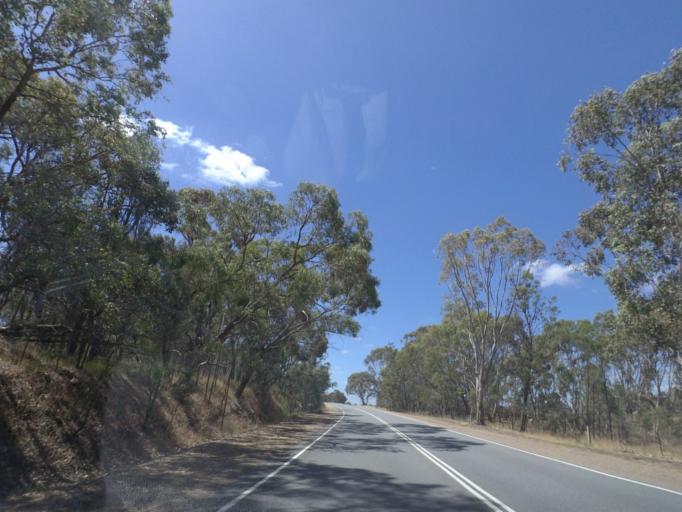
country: AU
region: Victoria
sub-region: Wangaratta
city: Wangaratta
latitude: -36.4592
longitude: 146.2350
